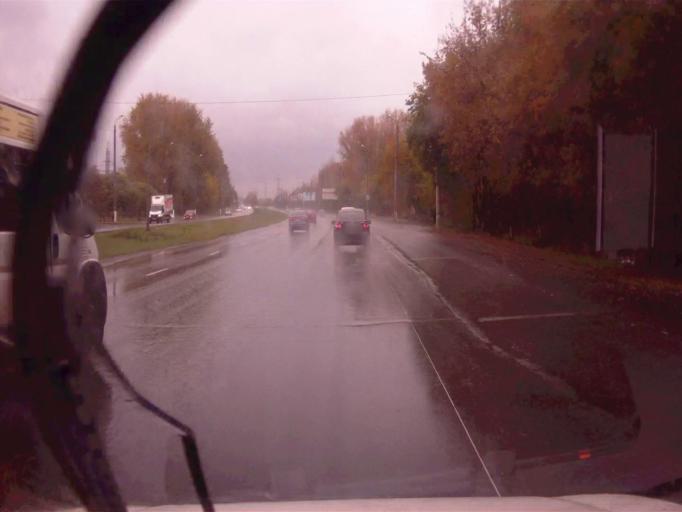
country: RU
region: Chelyabinsk
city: Dolgoderevenskoye
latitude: 55.2421
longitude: 61.3609
